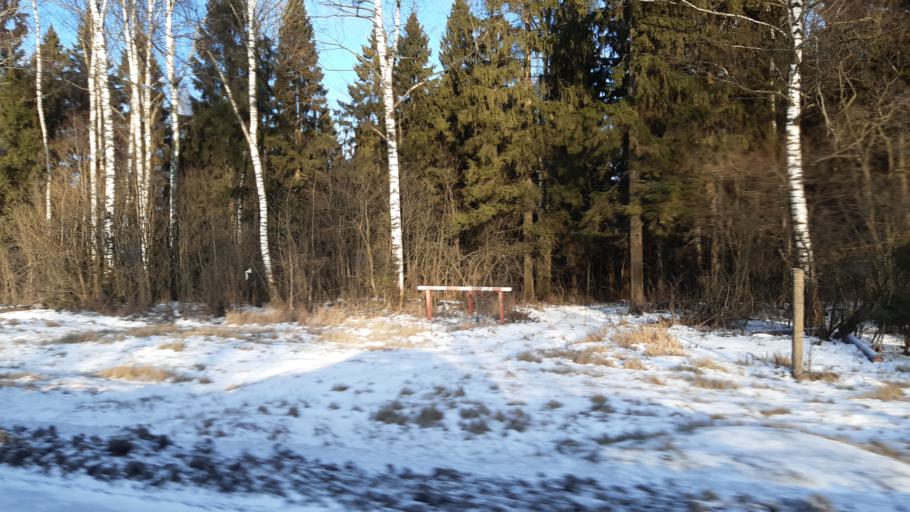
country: RU
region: Vladimir
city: Arsaki
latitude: 56.2811
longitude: 38.4007
